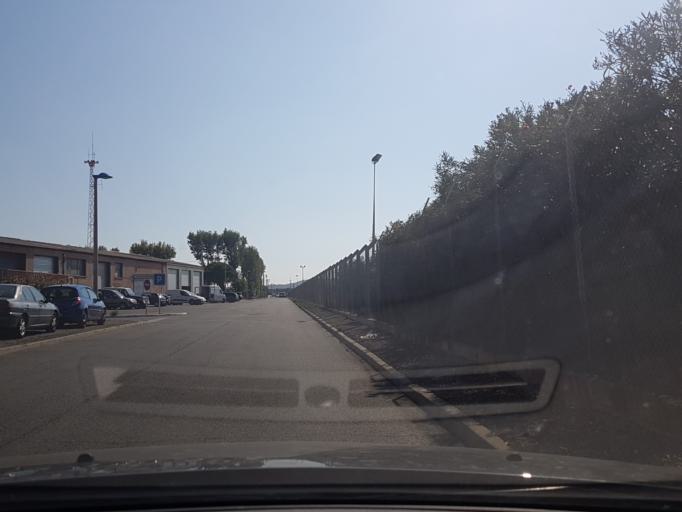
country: FR
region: Languedoc-Roussillon
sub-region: Departement de l'Aude
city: Port-la-Nouvelle
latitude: 43.0186
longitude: 3.0428
